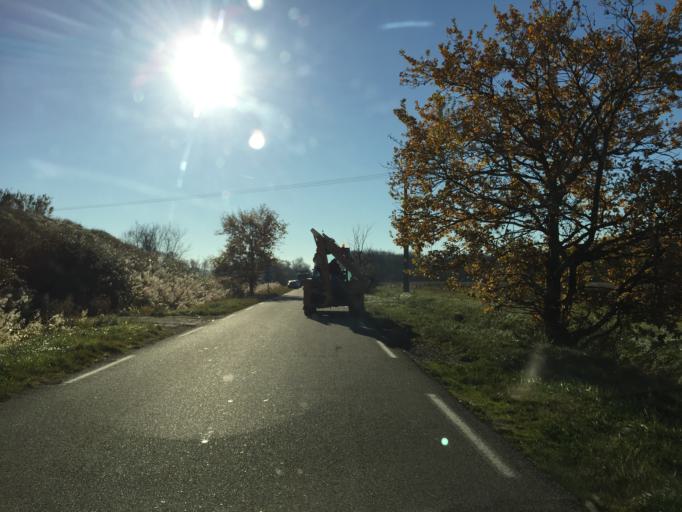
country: FR
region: Provence-Alpes-Cote d'Azur
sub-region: Departement du Vaucluse
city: Bedarrides
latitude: 44.0295
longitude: 4.9148
